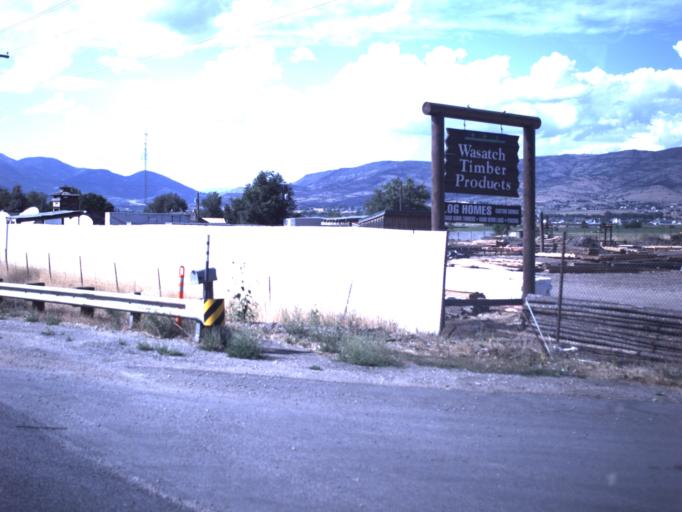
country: US
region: Utah
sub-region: Wasatch County
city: Heber
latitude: 40.4826
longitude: -111.4027
